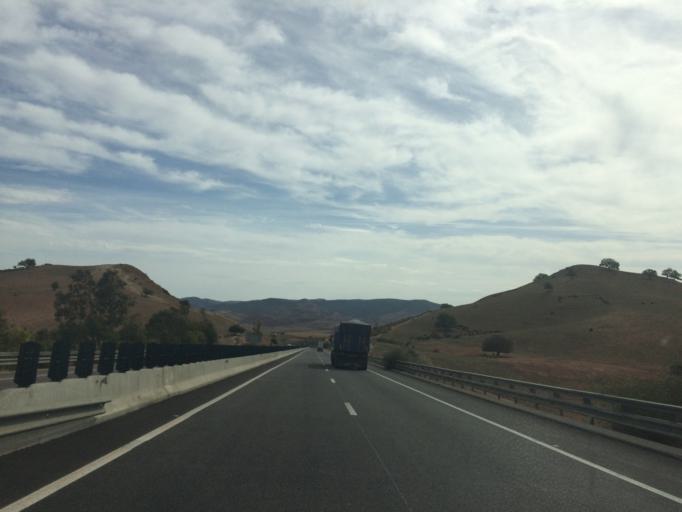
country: MA
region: Rabat-Sale-Zemmour-Zaer
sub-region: Khemisset
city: Khemisset
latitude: 33.7829
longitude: -5.9686
